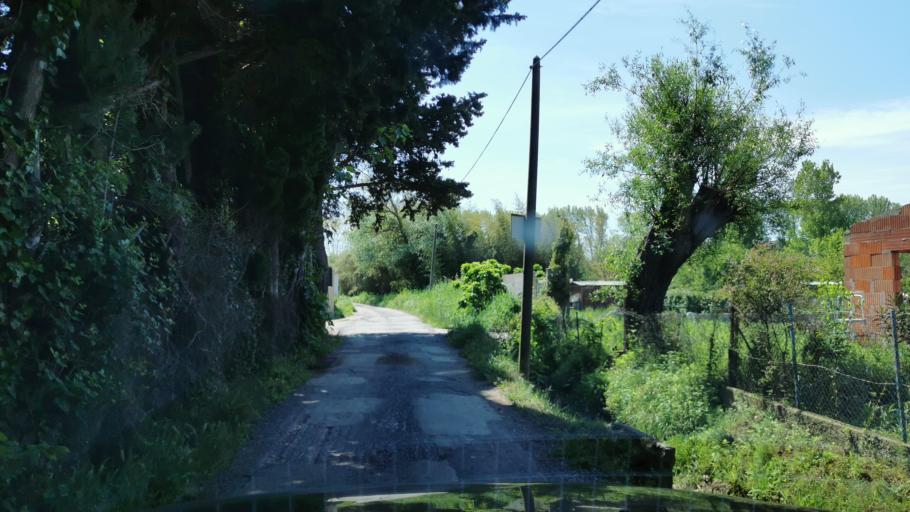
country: FR
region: Languedoc-Roussillon
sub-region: Departement de l'Aude
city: Narbonne
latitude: 43.1936
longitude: 3.0021
